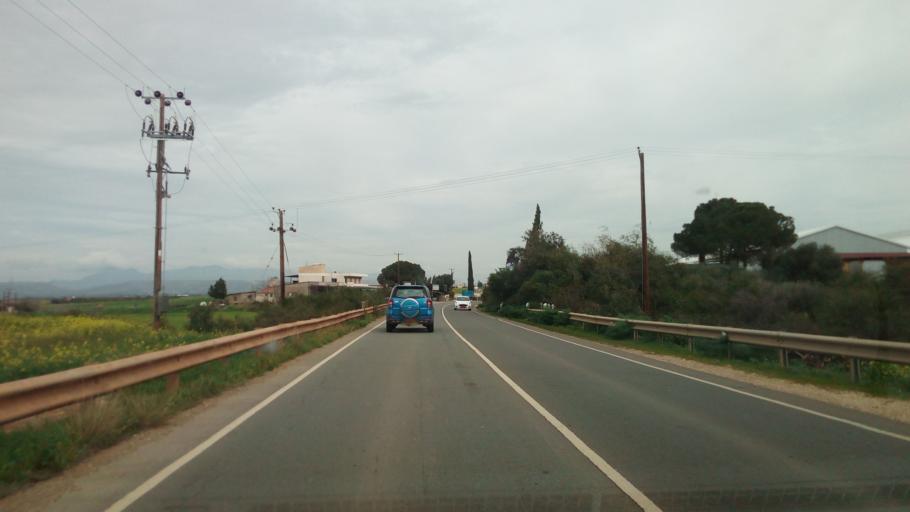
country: CY
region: Lefkosia
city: Astromeritis
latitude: 35.1335
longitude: 33.0190
